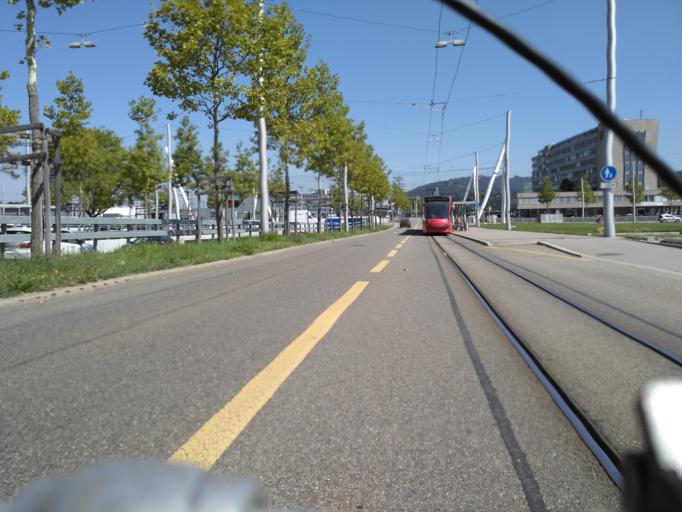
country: CH
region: Bern
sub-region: Bern-Mittelland District
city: Bern
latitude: 46.9637
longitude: 7.4674
